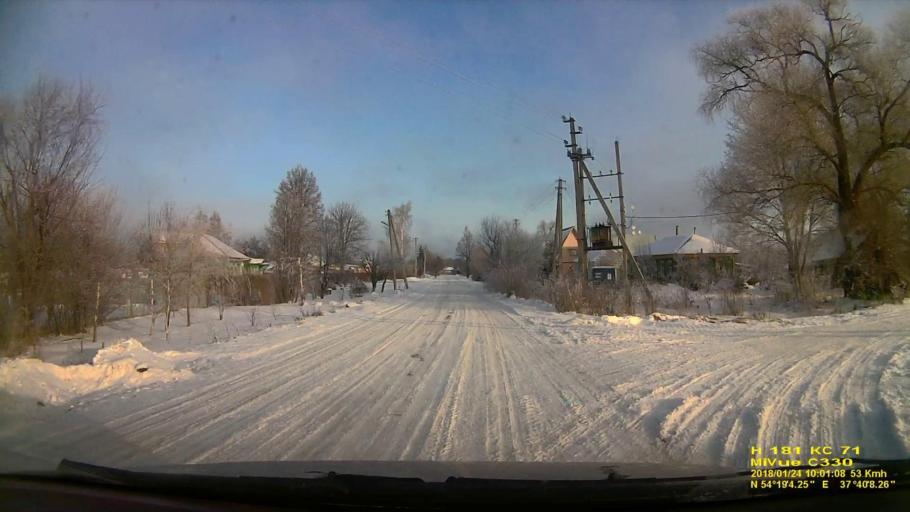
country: RU
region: Tula
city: Revyakino
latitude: 54.3179
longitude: 37.6690
